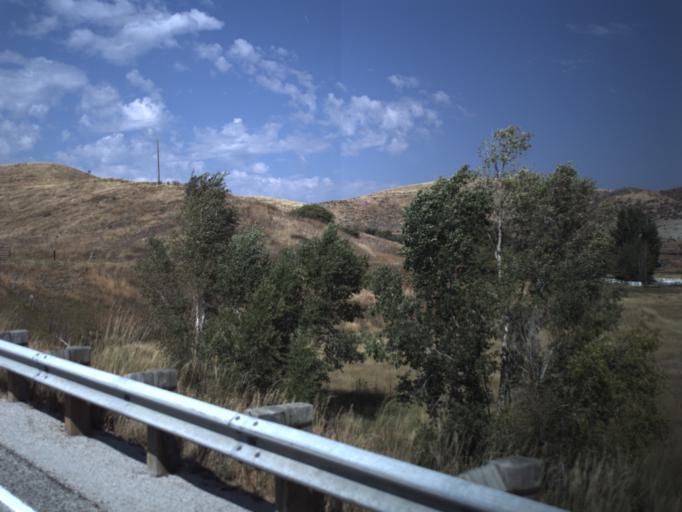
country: US
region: Utah
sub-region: Morgan County
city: Mountain Green
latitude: 41.1497
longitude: -111.7954
